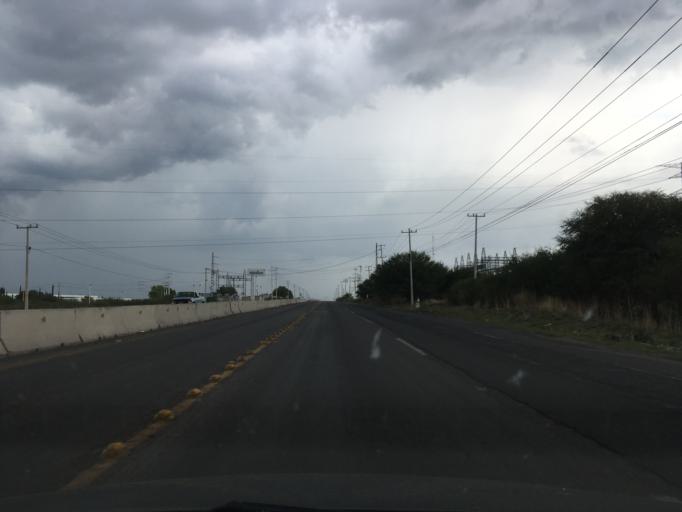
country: MX
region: Guanajuato
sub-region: Tarimoro
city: San Juan Bautista Cacalote
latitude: 20.3753
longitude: -100.7959
